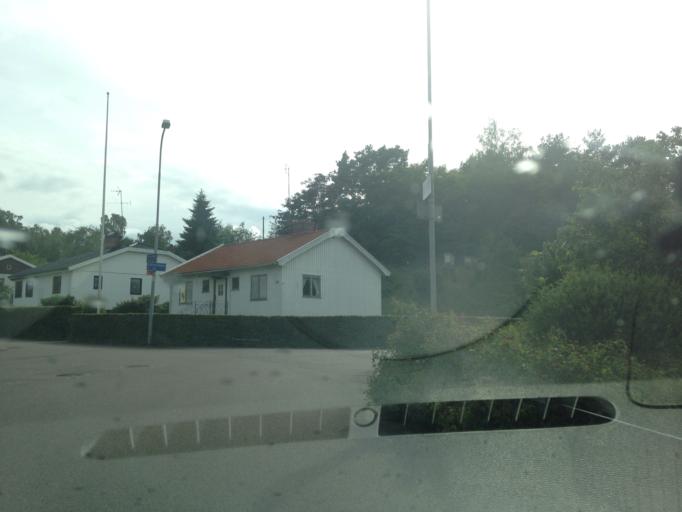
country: SE
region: Vaestra Goetaland
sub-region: Goteborg
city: Goeteborg
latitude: 57.7529
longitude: 11.9684
